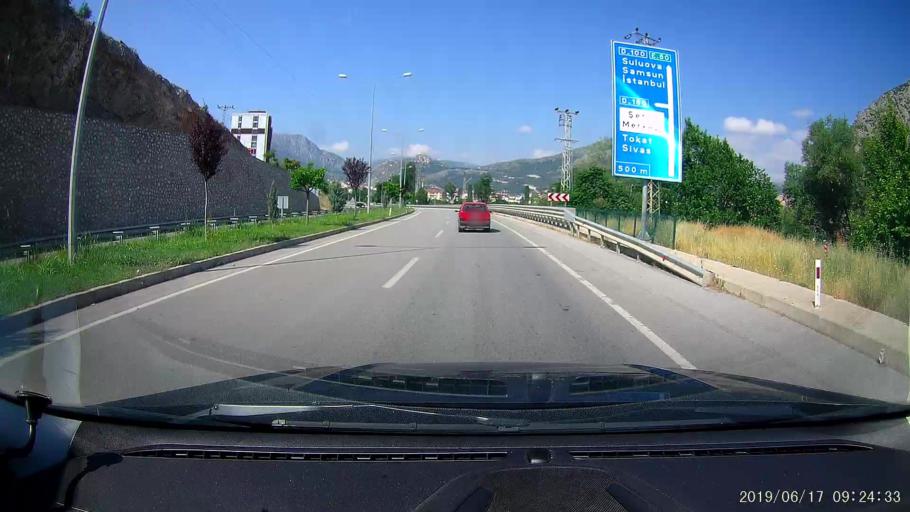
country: TR
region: Amasya
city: Amasya
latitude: 40.6716
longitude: 35.8558
